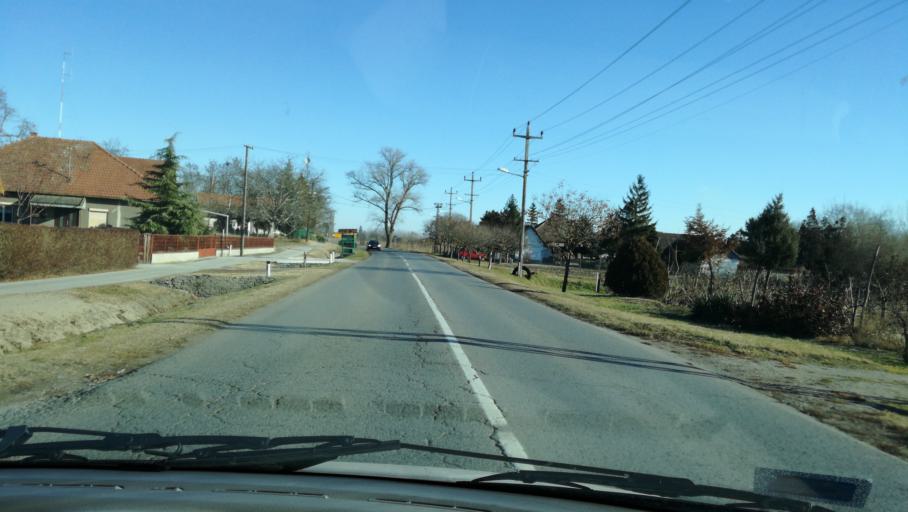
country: HU
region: Csongrad
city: Asotthalom
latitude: 46.1111
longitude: 19.8300
